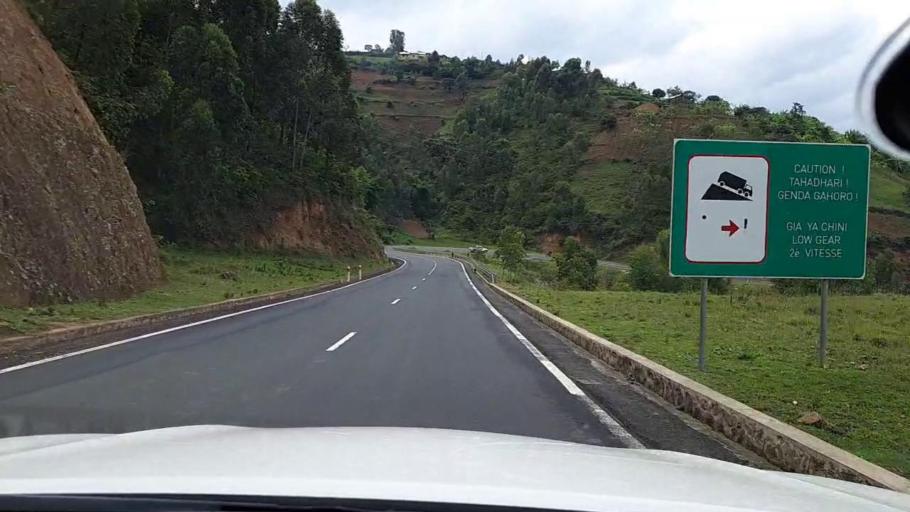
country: RW
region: Western Province
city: Kibuye
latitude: -2.1822
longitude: 29.2905
